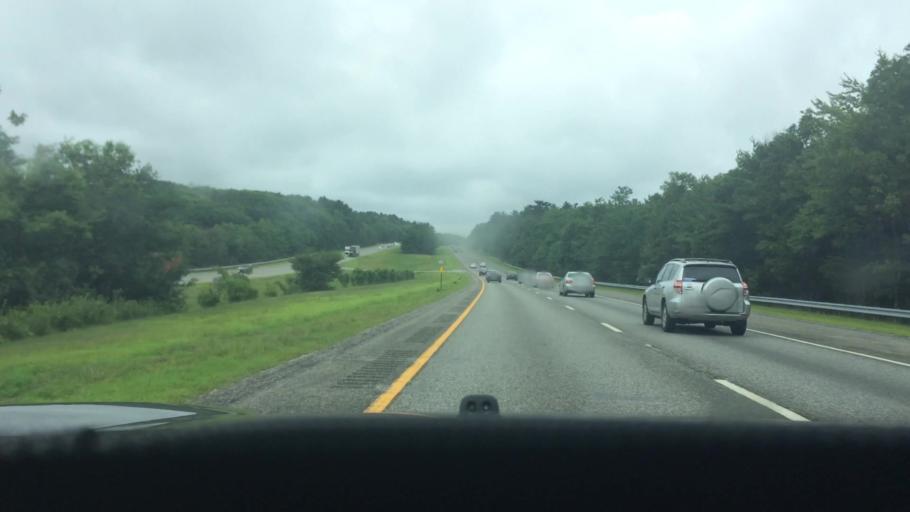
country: US
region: Rhode Island
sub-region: Kent County
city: West Greenwich
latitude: 41.6289
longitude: -71.6373
